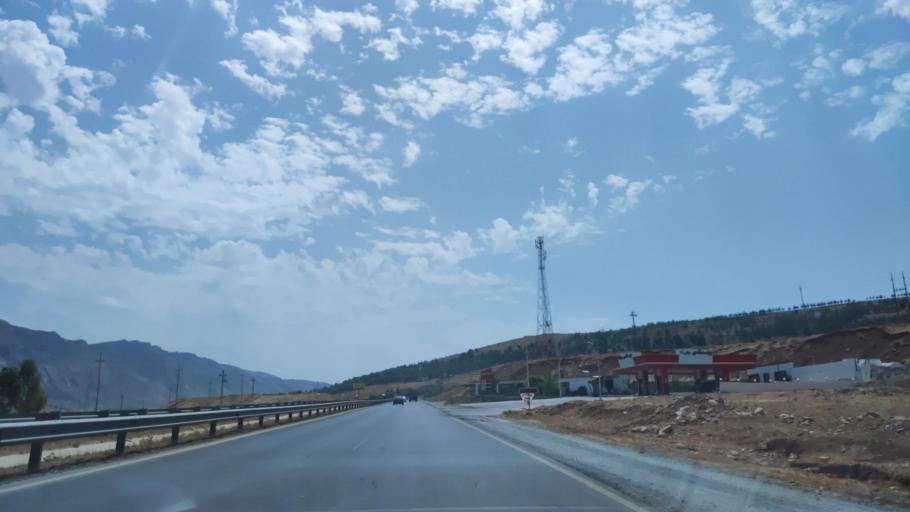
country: IQ
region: Arbil
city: Shaqlawah
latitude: 36.4968
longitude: 44.3641
